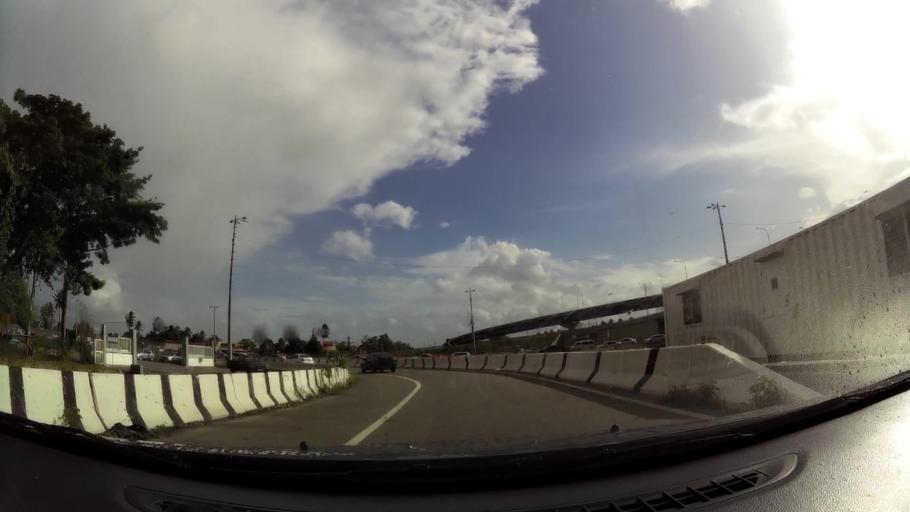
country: TT
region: Tunapuna/Piarco
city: Tunapuna
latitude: 10.6334
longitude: -61.4292
